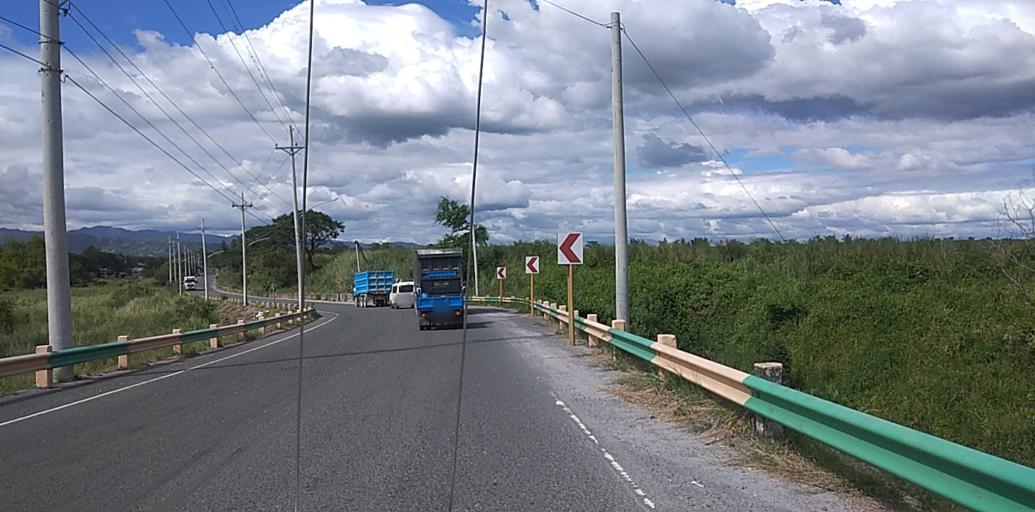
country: PH
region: Central Luzon
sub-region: Province of Pampanga
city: Dolores
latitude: 15.0878
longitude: 120.5392
